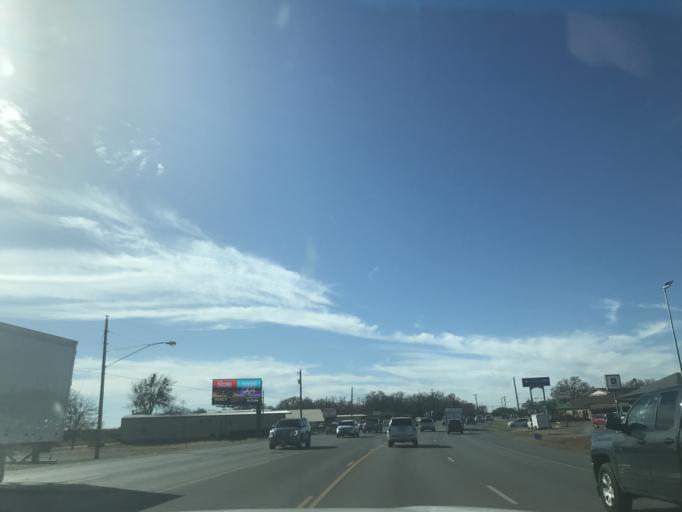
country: US
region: Texas
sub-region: Erath County
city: Stephenville
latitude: 32.2046
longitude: -98.2115
